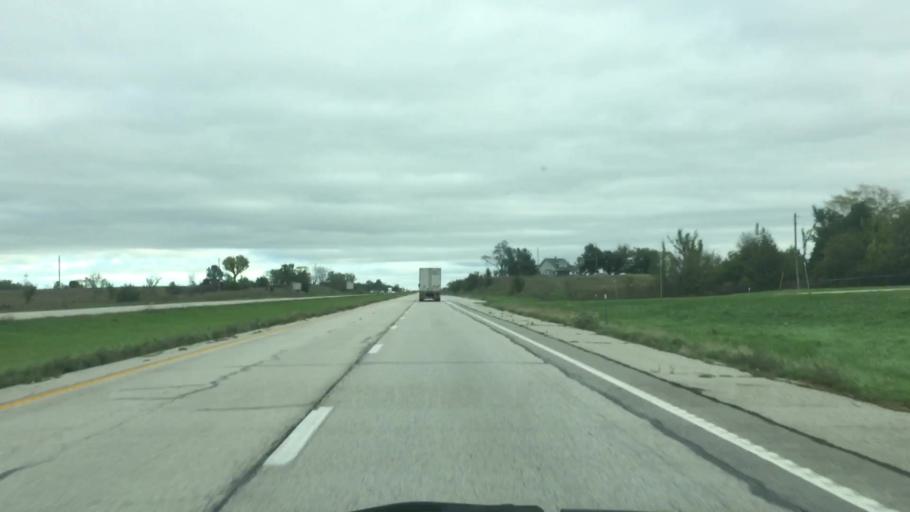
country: US
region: Missouri
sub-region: Harrison County
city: Bethany
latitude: 40.1176
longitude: -94.0606
